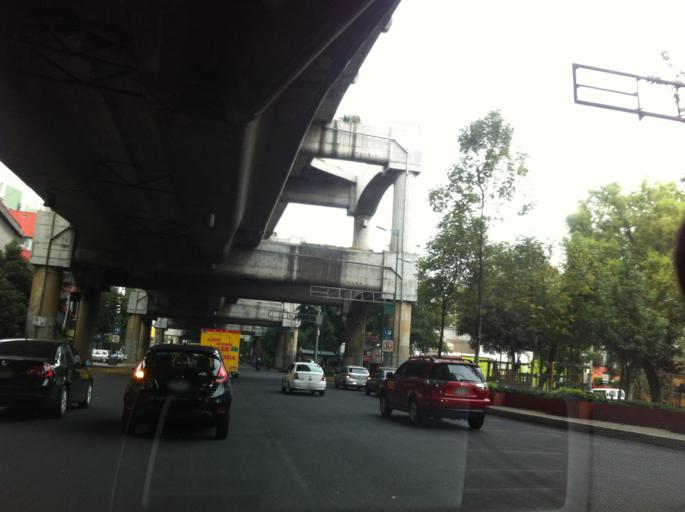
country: MX
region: Mexico City
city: Colonia del Valle
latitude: 19.3851
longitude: -99.1832
